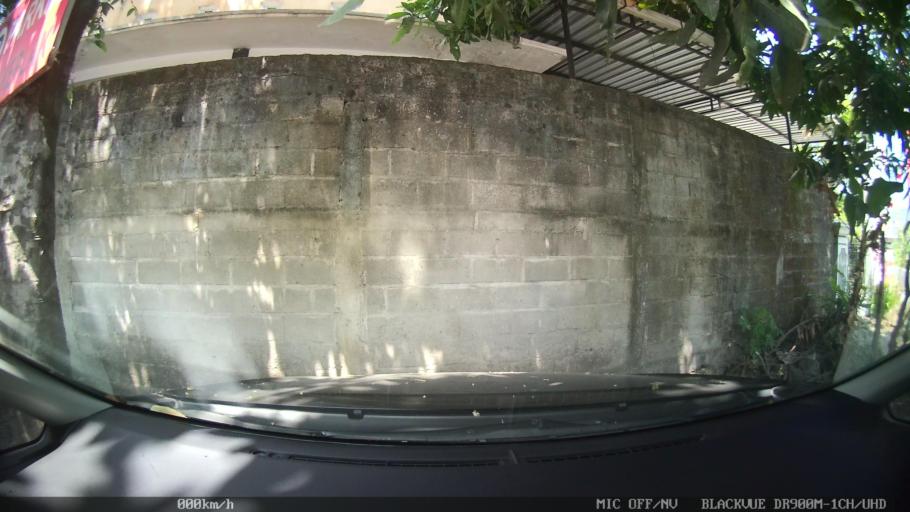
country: ID
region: Daerah Istimewa Yogyakarta
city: Pundong
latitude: -7.9388
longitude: 110.3741
